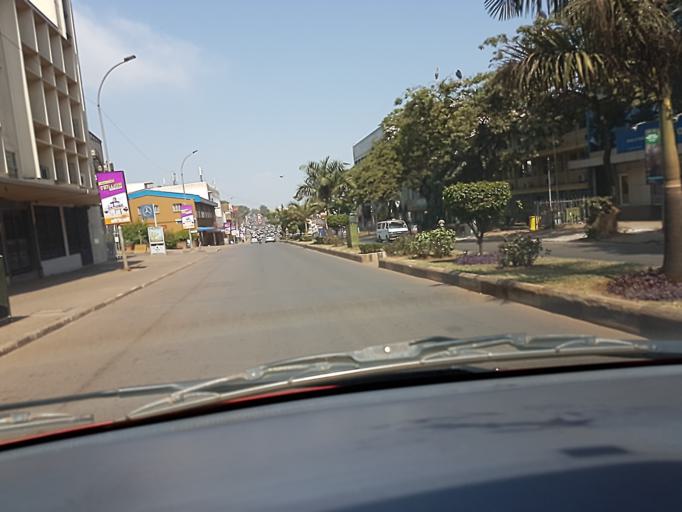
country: UG
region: Central Region
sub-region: Kampala District
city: Kampala
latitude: 0.3151
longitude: 32.5910
